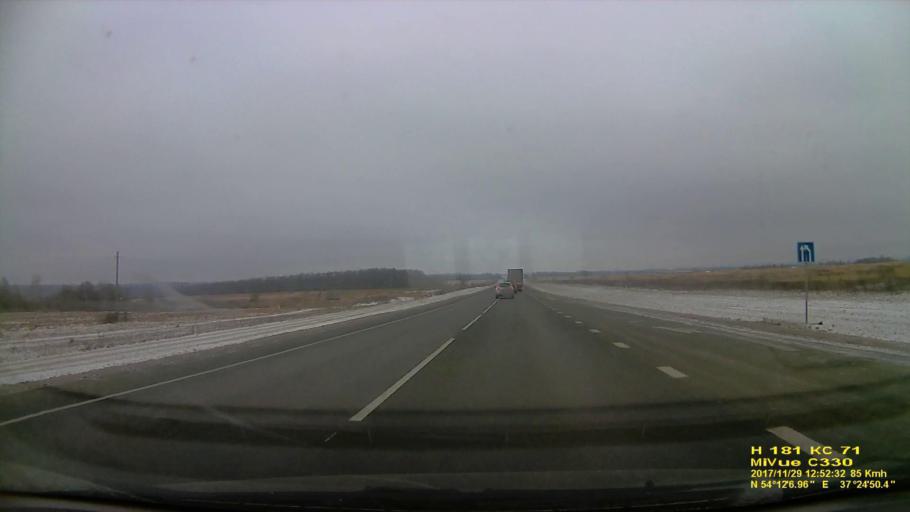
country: RU
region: Tula
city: Leninskiy
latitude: 54.2020
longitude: 37.4139
